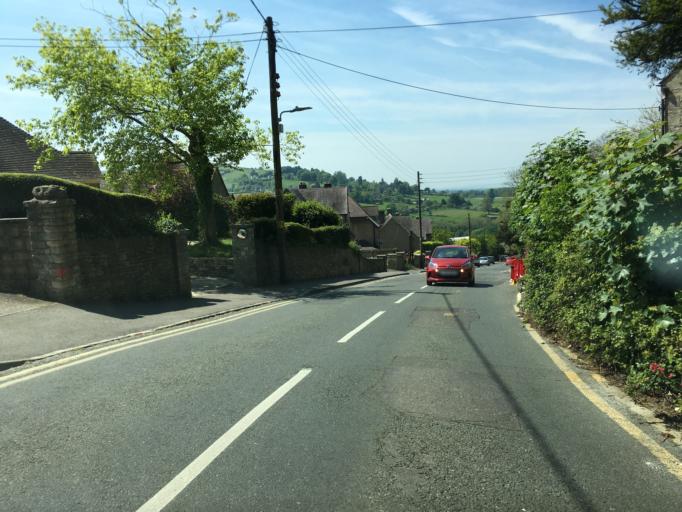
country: GB
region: England
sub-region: Gloucestershire
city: Stroud
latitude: 51.7382
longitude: -2.2273
